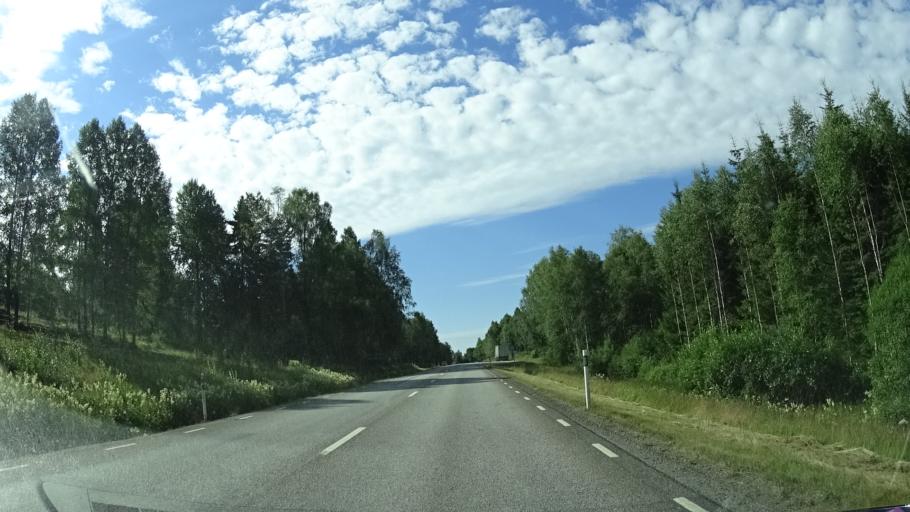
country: SE
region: Vaermland
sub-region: Arjangs Kommun
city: Arjaeng
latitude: 59.4078
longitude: 12.1271
